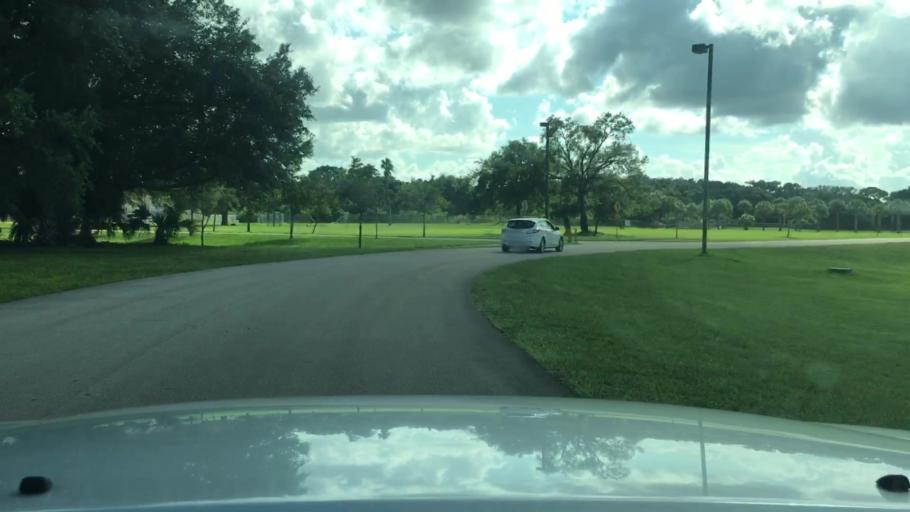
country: US
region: Florida
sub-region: Miami-Dade County
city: Ives Estates
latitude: 25.9695
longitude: -80.1690
